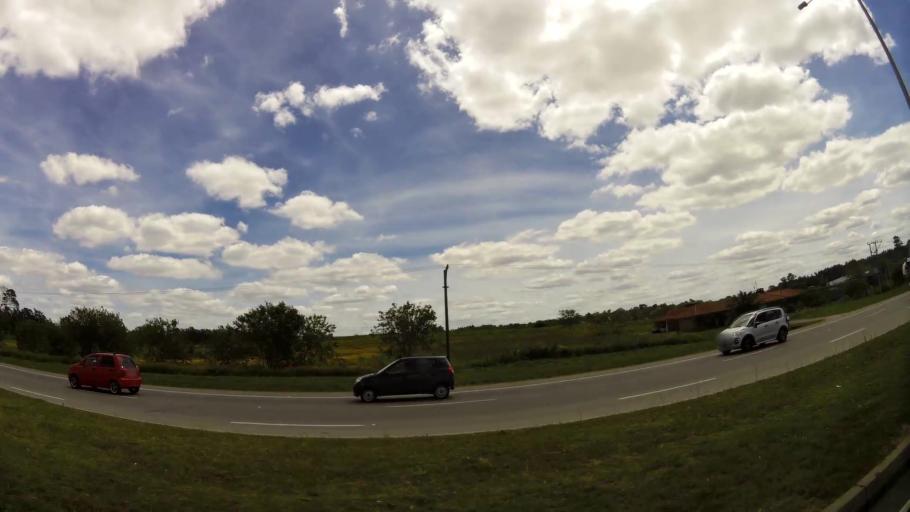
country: UY
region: Canelones
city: Colonia Nicolich
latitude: -34.8255
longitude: -55.9980
